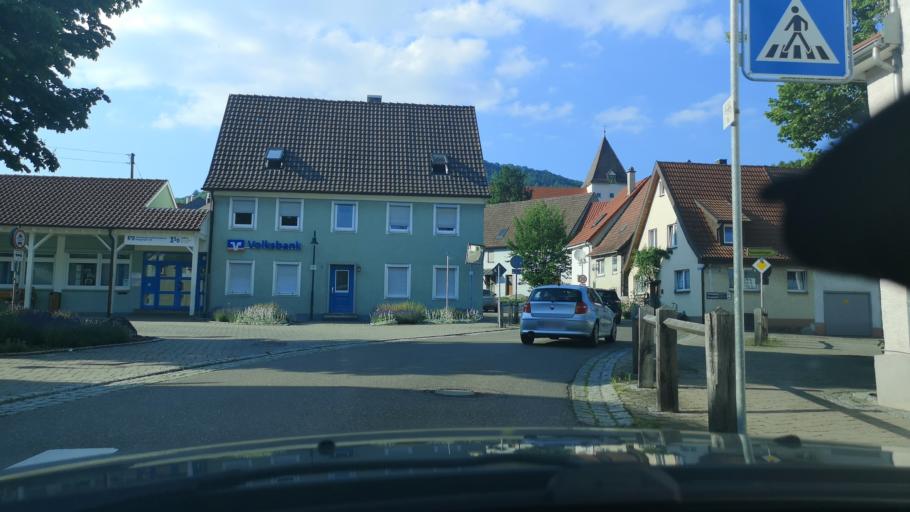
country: DE
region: Baden-Wuerttemberg
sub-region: Regierungsbezirk Stuttgart
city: Deggingen
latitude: 48.6170
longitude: 9.7356
